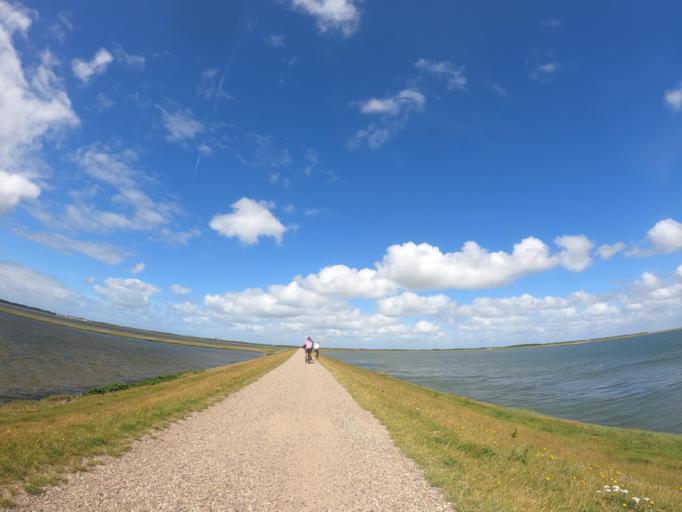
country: DE
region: Schleswig-Holstein
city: Tinnum
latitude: 54.8668
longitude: 8.3335
